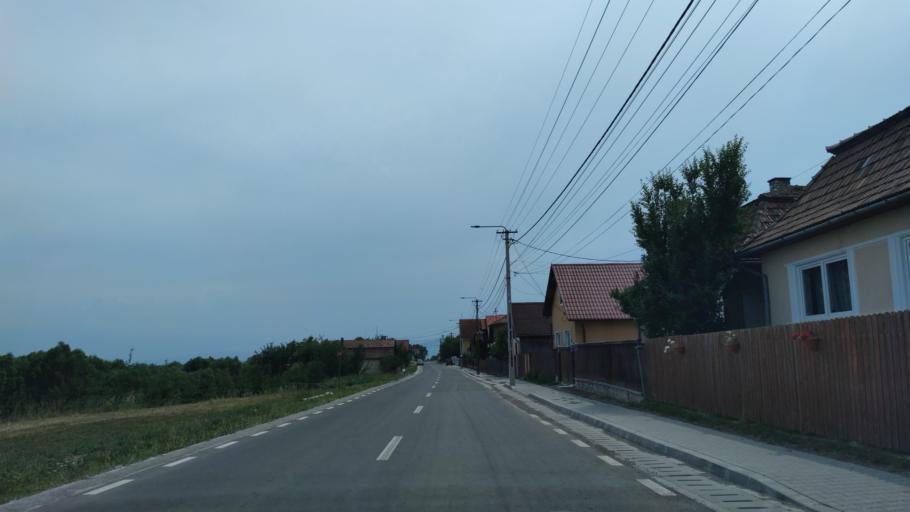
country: RO
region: Harghita
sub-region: Comuna Remetea
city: Remetea
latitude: 46.8091
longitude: 25.4596
